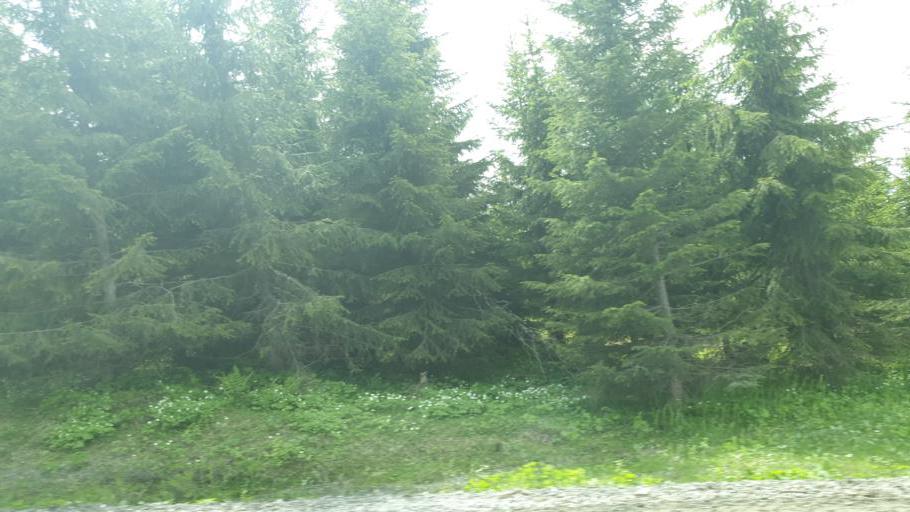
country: NO
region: Nord-Trondelag
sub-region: Leksvik
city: Leksvik
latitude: 63.6914
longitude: 10.4593
